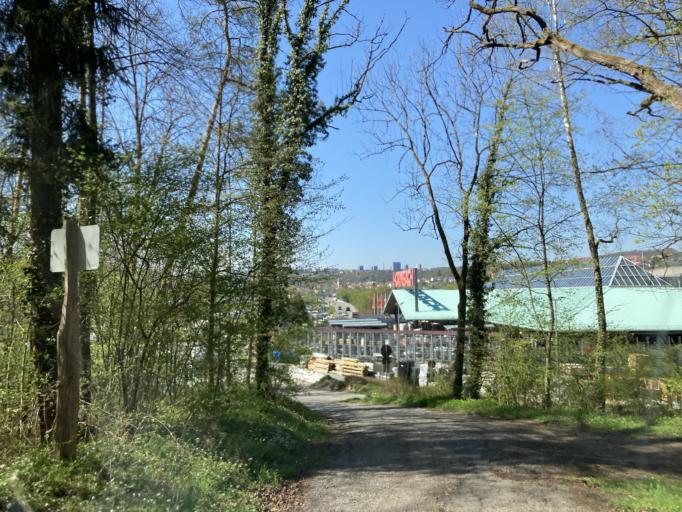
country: DE
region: Baden-Wuerttemberg
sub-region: Tuebingen Region
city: Kusterdingen
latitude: 48.5211
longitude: 9.0988
